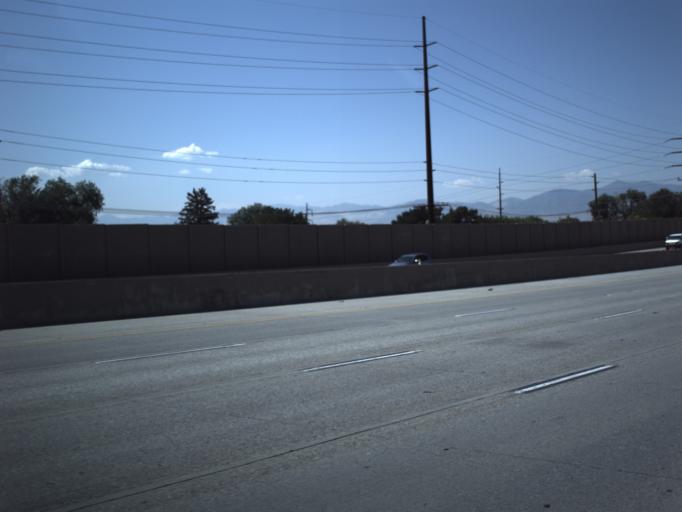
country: US
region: Utah
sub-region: Salt Lake County
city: South Salt Lake
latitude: 40.7197
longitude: -111.8631
